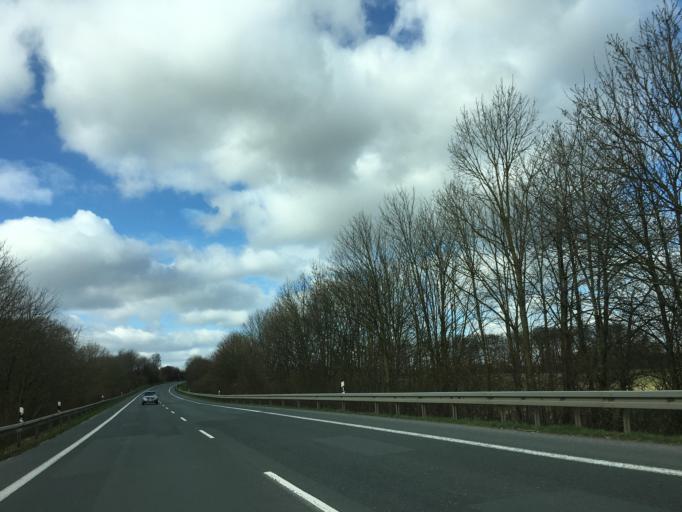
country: DE
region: North Rhine-Westphalia
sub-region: Regierungsbezirk Munster
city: Horstmar
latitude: 52.0738
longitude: 7.3046
